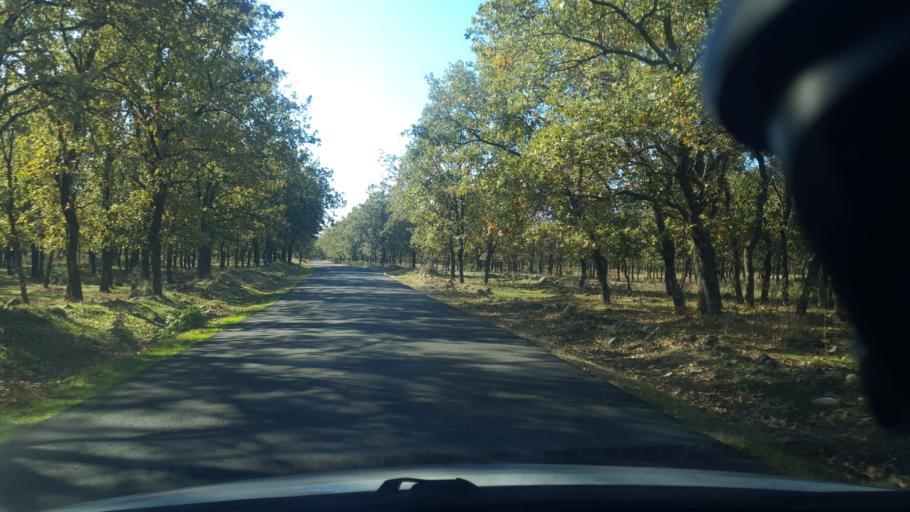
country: ES
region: Castille and Leon
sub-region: Provincia de Avila
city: Candeleda
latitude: 40.1327
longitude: -5.2645
